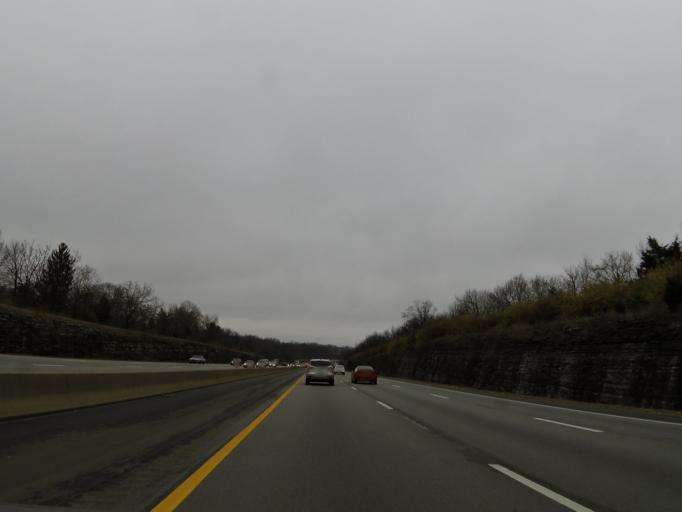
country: US
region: Kentucky
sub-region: Scott County
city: Georgetown
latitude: 38.2002
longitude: -84.5277
